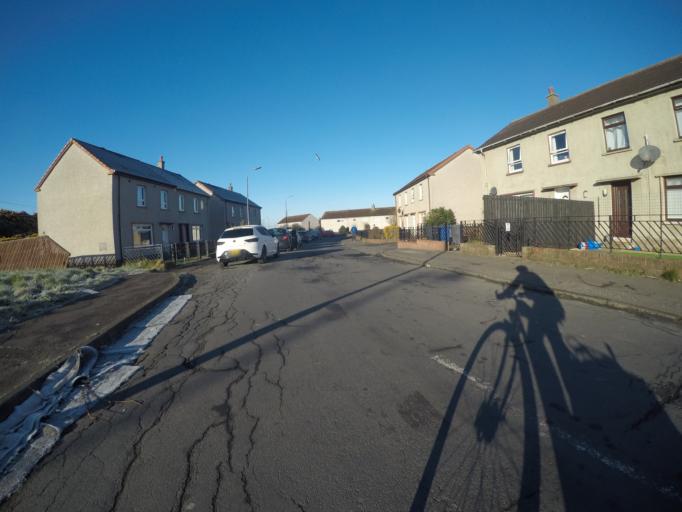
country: GB
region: Scotland
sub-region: North Ayrshire
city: Stevenston
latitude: 55.6298
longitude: -4.7390
